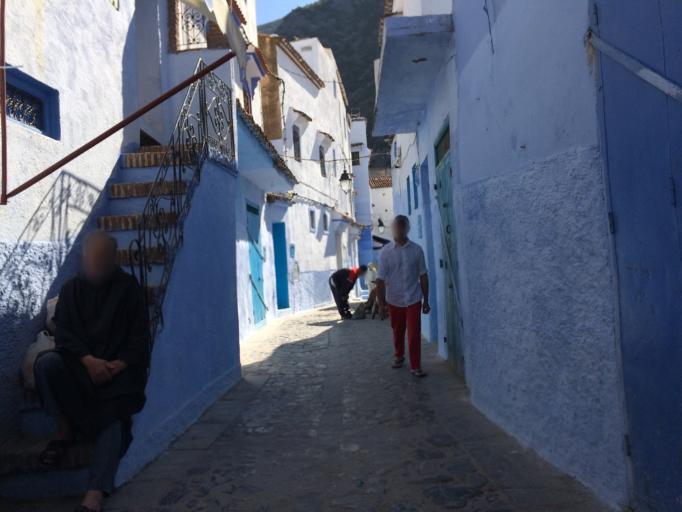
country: MA
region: Tanger-Tetouan
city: Chefchaouene
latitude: 35.1703
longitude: -5.2584
